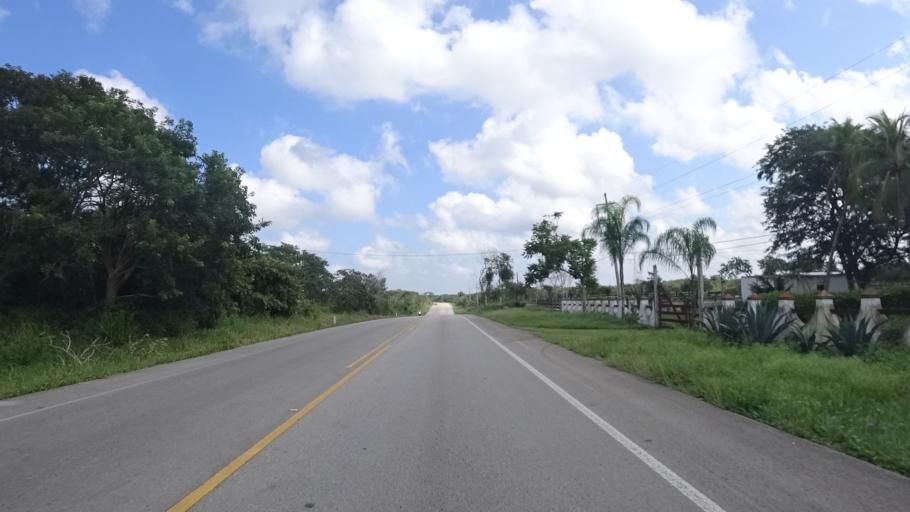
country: MX
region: Yucatan
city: Espita
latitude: 20.9916
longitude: -88.1755
